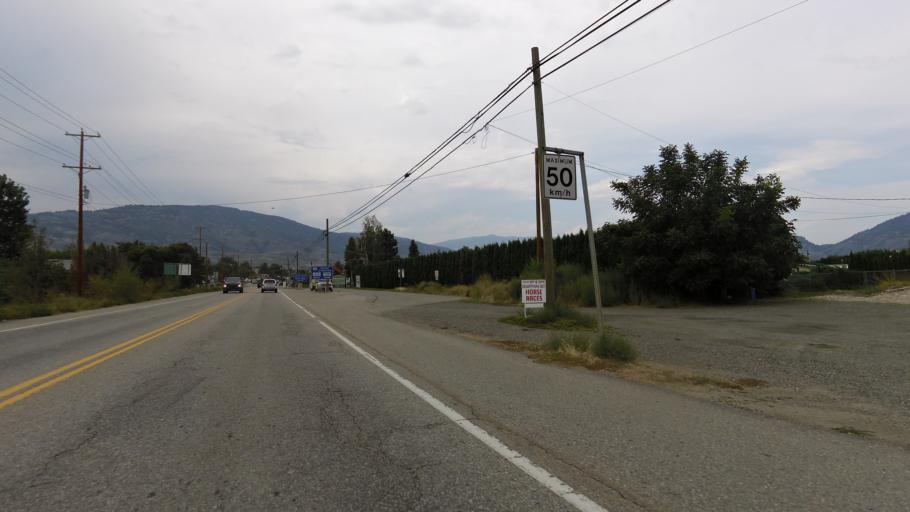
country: CA
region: British Columbia
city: Osoyoos
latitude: 49.0280
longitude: -119.4386
